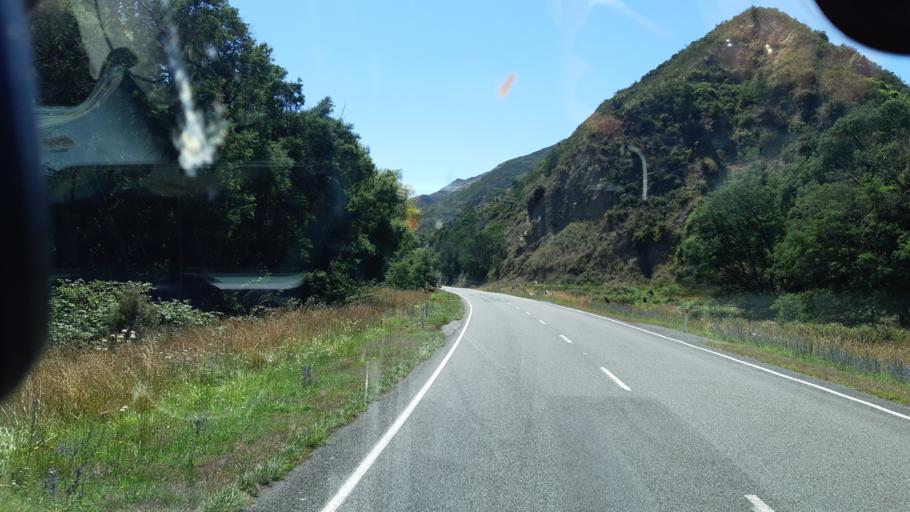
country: NZ
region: Canterbury
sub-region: Kaikoura District
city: Kaikoura
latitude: -42.6366
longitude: 173.3436
